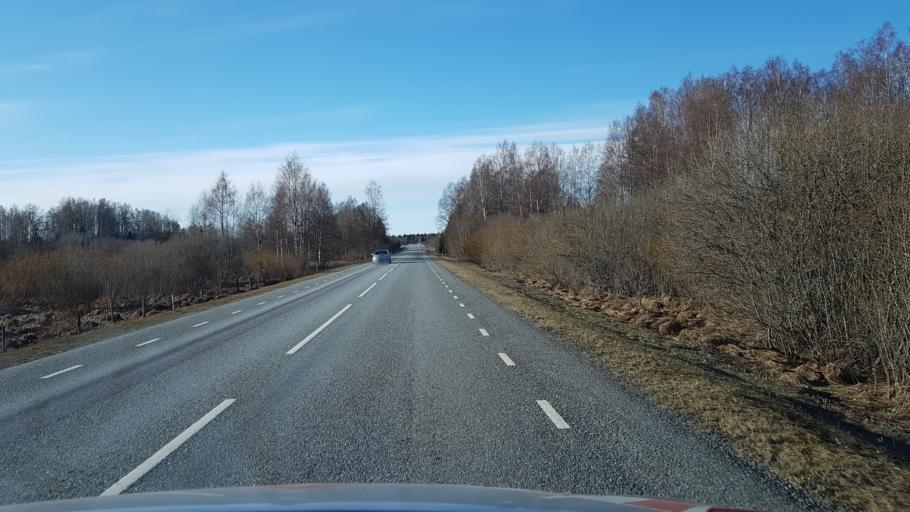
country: EE
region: Laeaene-Virumaa
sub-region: Tapa vald
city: Tapa
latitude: 59.4469
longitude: 25.9496
